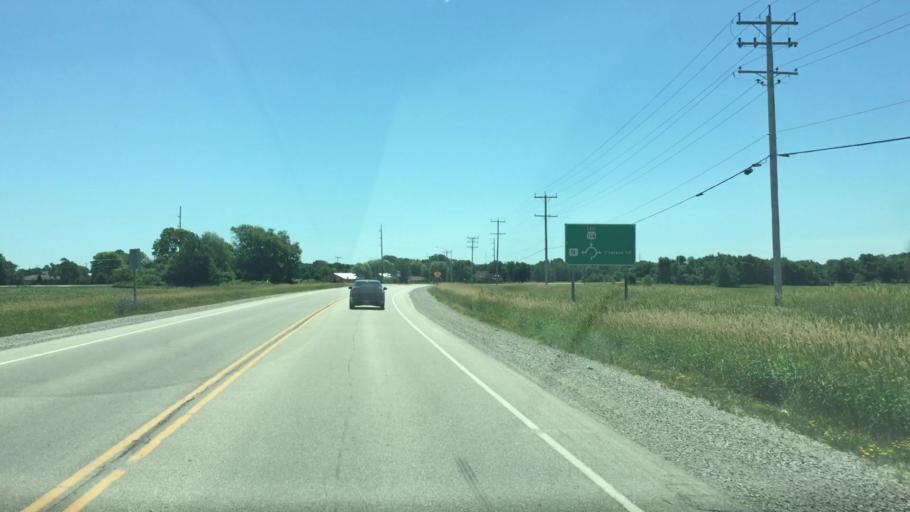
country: US
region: Wisconsin
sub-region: Outagamie County
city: Combined Locks
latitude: 44.2028
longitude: -88.3271
